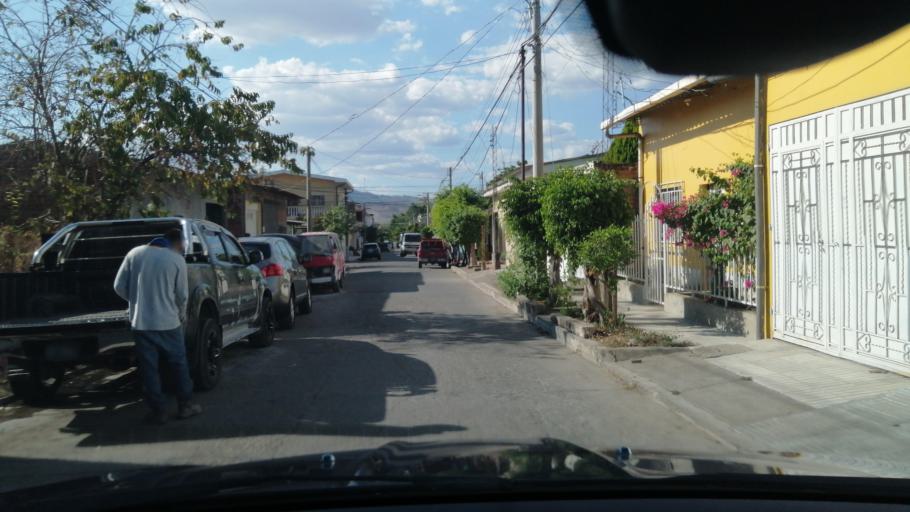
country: SV
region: Santa Ana
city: Metapan
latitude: 14.3326
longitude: -89.4416
